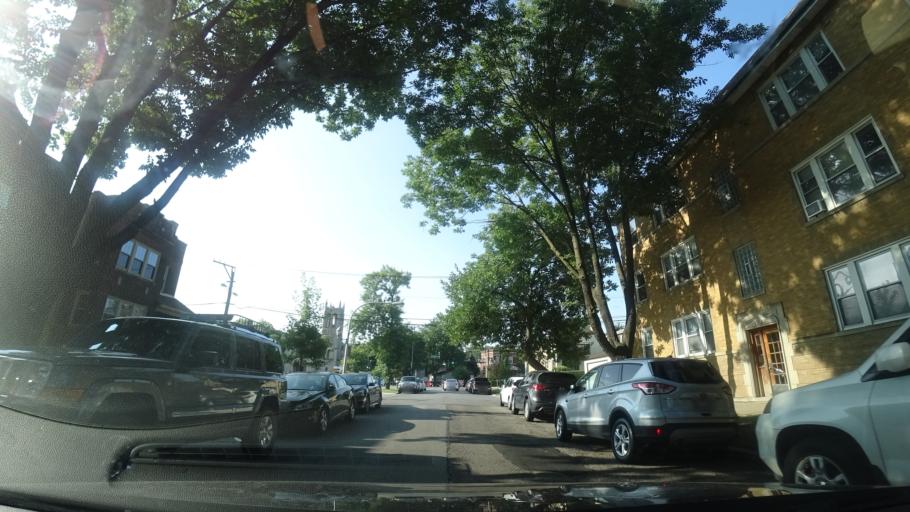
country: US
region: Illinois
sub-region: Cook County
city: Lincolnwood
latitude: 41.9614
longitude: -87.7525
